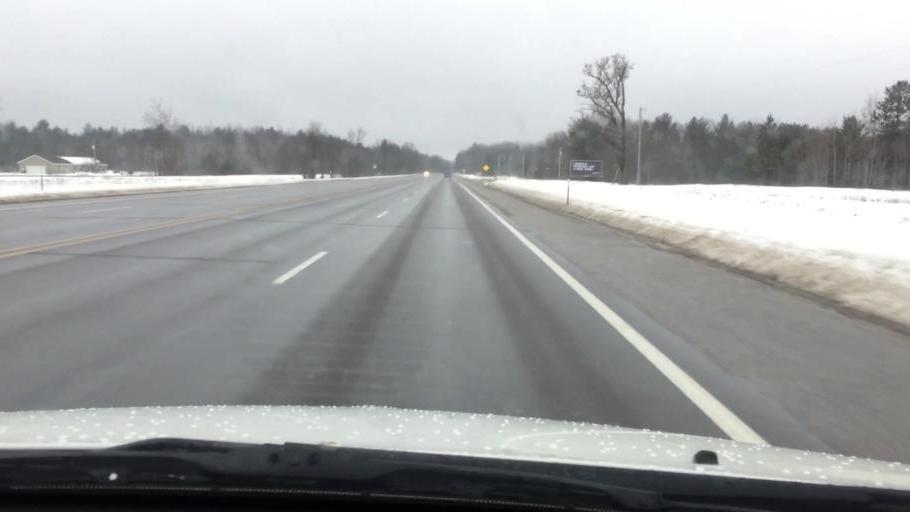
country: US
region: Michigan
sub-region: Kalkaska County
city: Kalkaska
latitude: 44.6706
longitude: -85.2402
